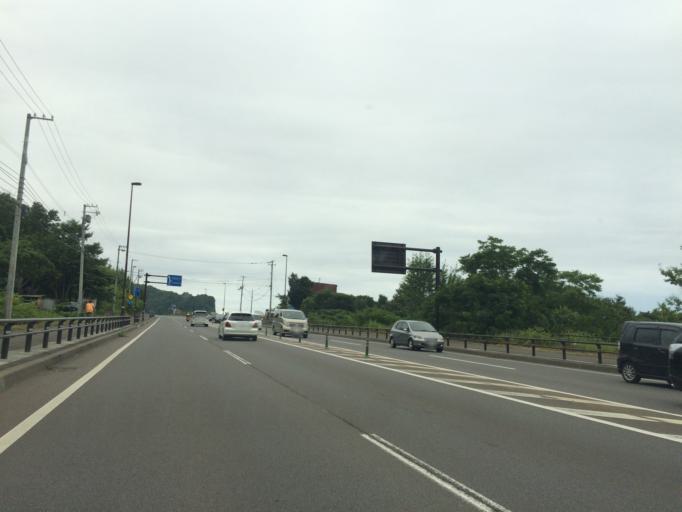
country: JP
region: Hokkaido
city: Otaru
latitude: 43.1520
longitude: 141.1306
